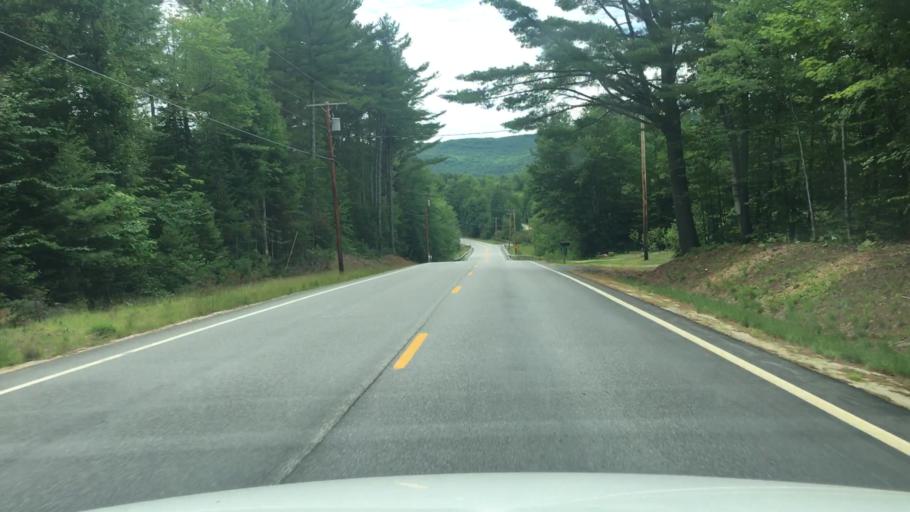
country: US
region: Maine
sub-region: Oxford County
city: West Paris
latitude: 44.3673
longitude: -70.4937
